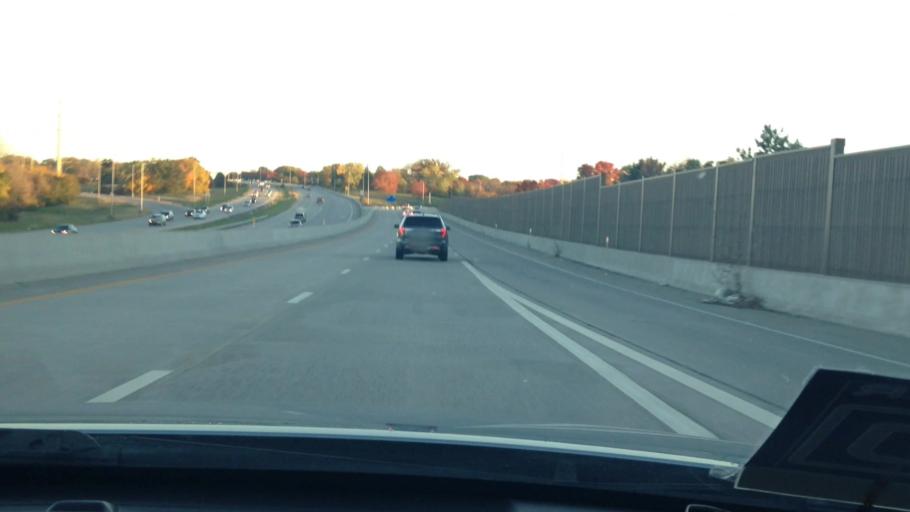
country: US
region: Kansas
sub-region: Johnson County
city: Lenexa
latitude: 38.9171
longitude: -94.7026
